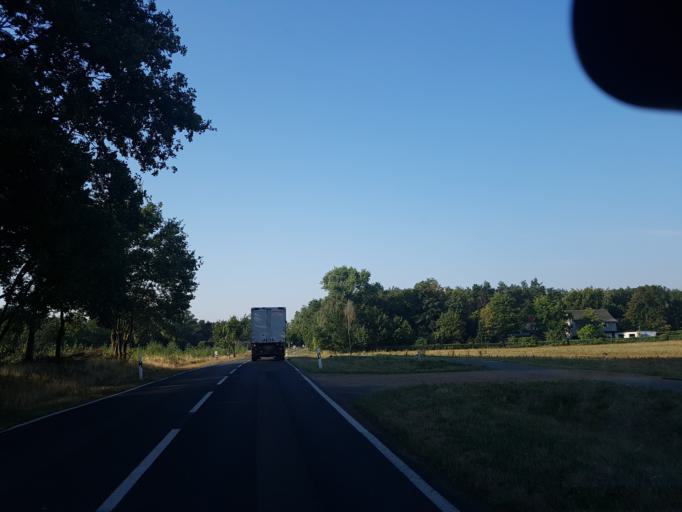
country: DE
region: Brandenburg
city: Hohenleipisch
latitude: 51.4758
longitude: 13.5496
